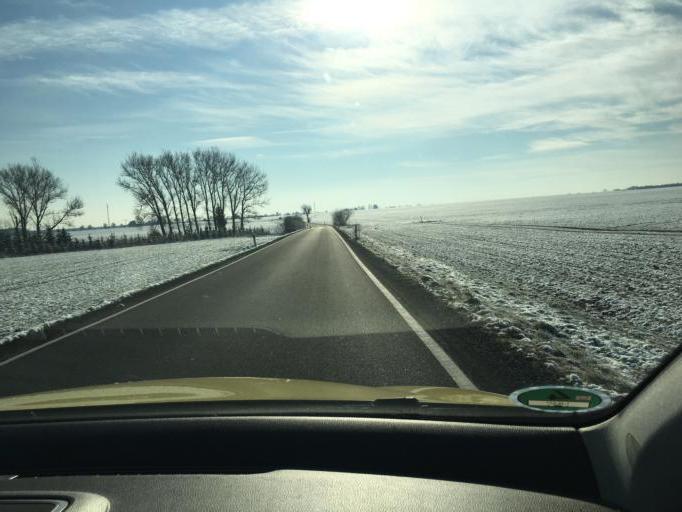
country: DE
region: Saxony
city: Belgershain
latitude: 51.2527
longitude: 12.5406
